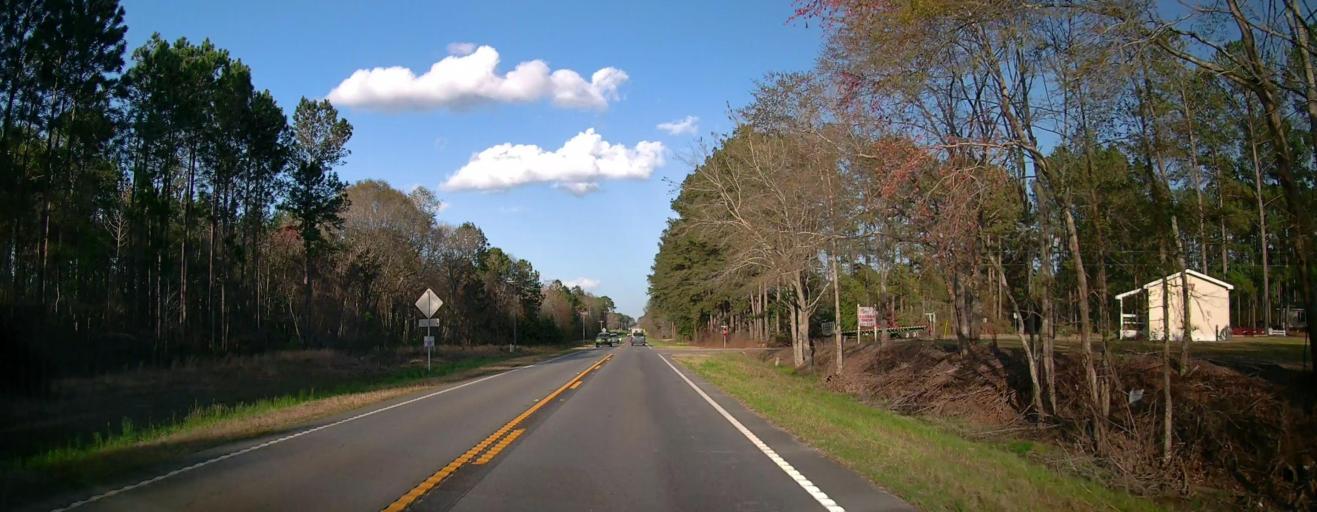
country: US
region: Georgia
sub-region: Tattnall County
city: Reidsville
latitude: 32.1234
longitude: -82.0628
